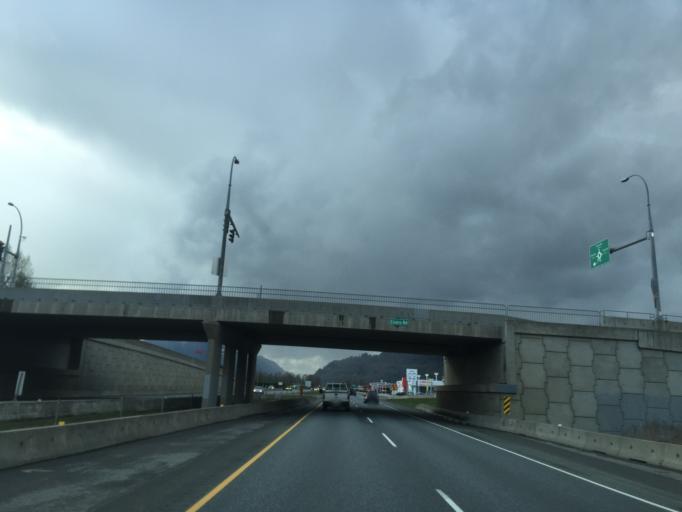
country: CA
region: British Columbia
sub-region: Fraser Valley Regional District
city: Chilliwack
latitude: 49.1439
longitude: -121.9768
